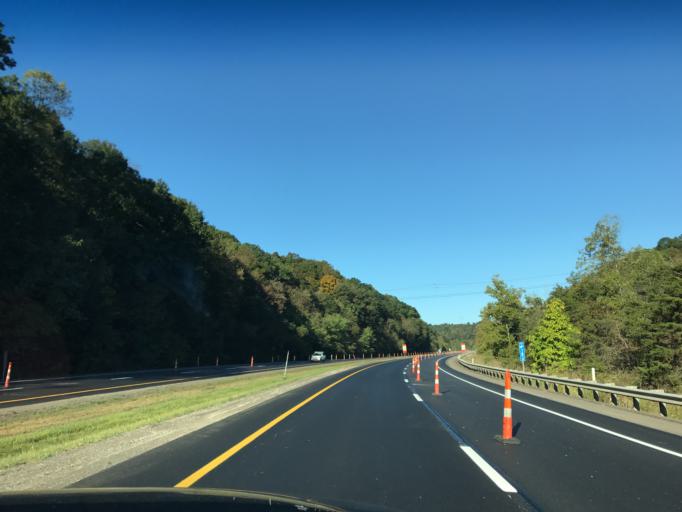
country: US
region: Ohio
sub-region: Washington County
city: Reno
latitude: 39.2443
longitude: -81.3690
